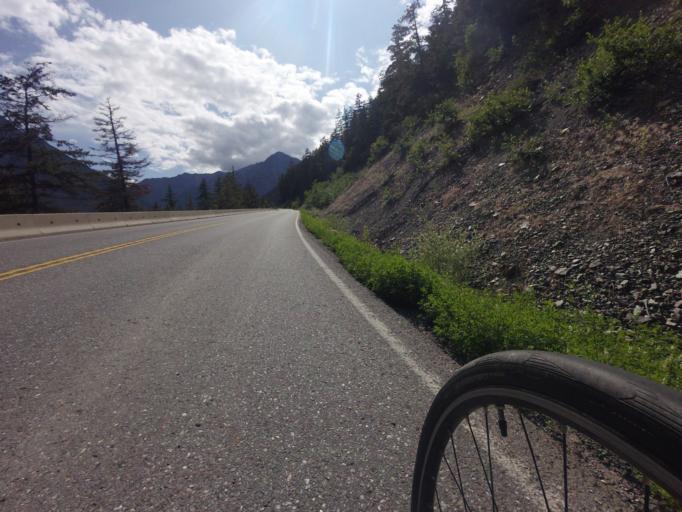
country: CA
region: British Columbia
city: Lillooet
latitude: 50.6526
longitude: -122.0143
